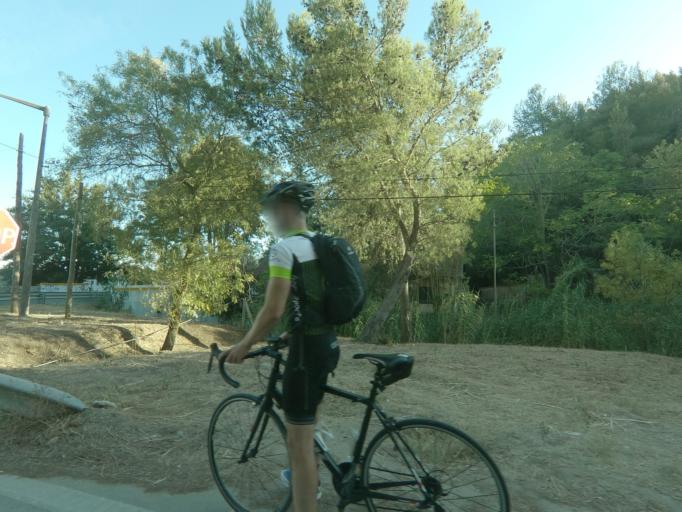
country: PT
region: Setubal
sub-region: Setubal
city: Setubal
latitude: 38.5044
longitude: -8.9284
